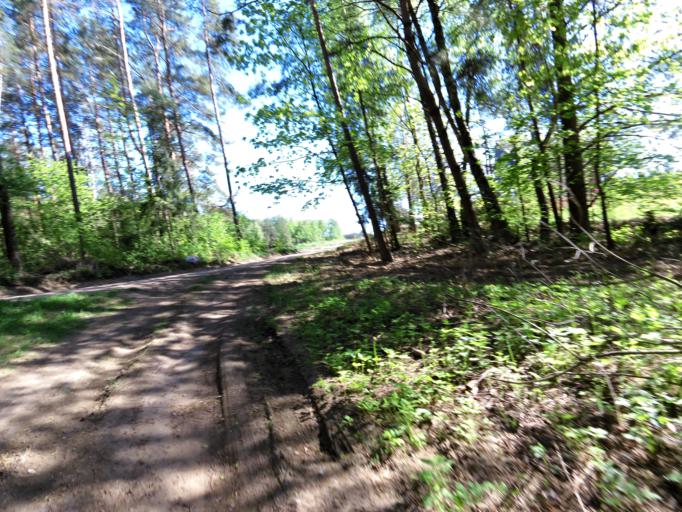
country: LT
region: Vilnius County
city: Pilaite
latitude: 54.6877
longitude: 25.1627
